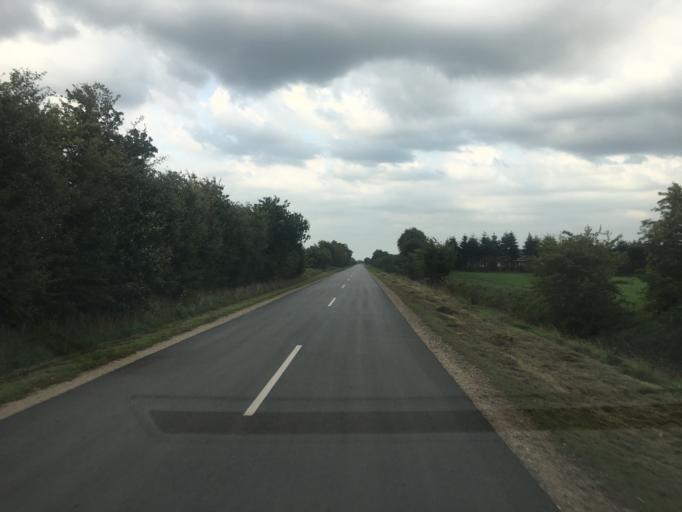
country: DK
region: South Denmark
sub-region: Tonder Kommune
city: Logumkloster
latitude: 55.0623
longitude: 9.0337
